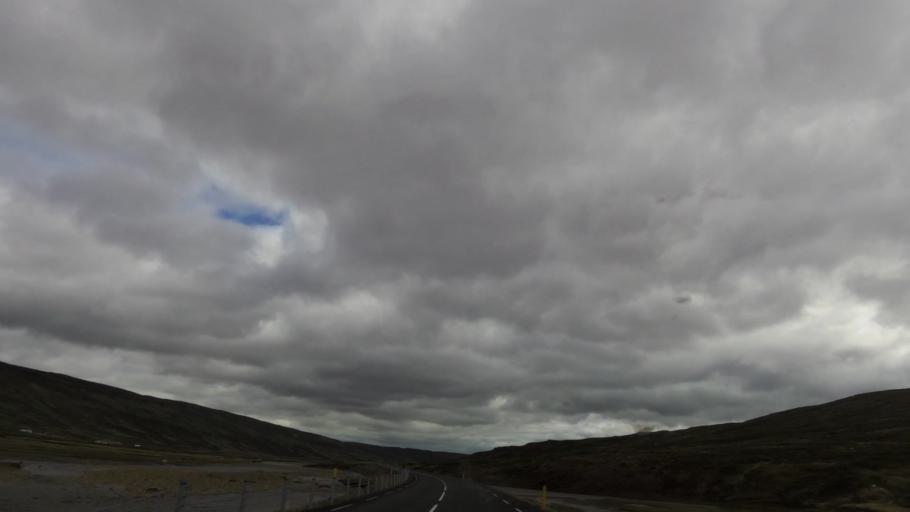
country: IS
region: West
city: Stykkisholmur
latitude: 65.7583
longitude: -21.8619
